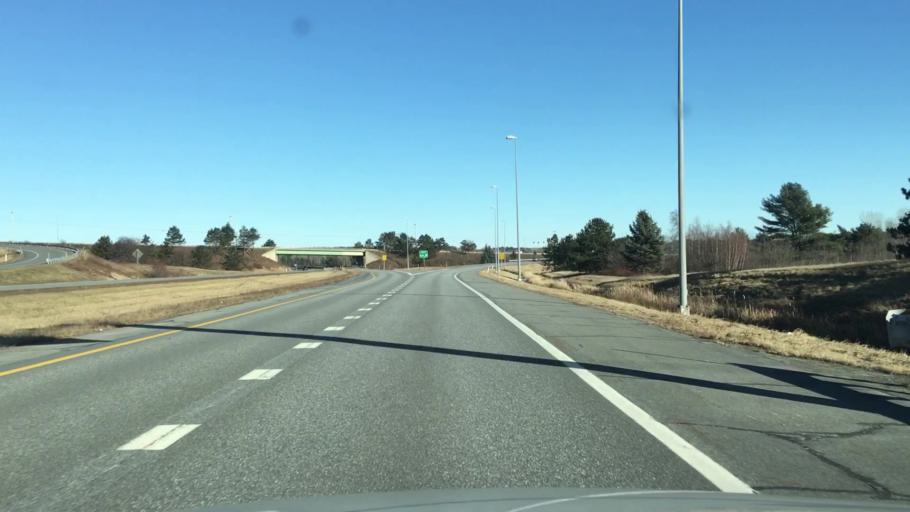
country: US
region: Maine
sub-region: Penobscot County
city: Brewer
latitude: 44.7691
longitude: -68.7252
